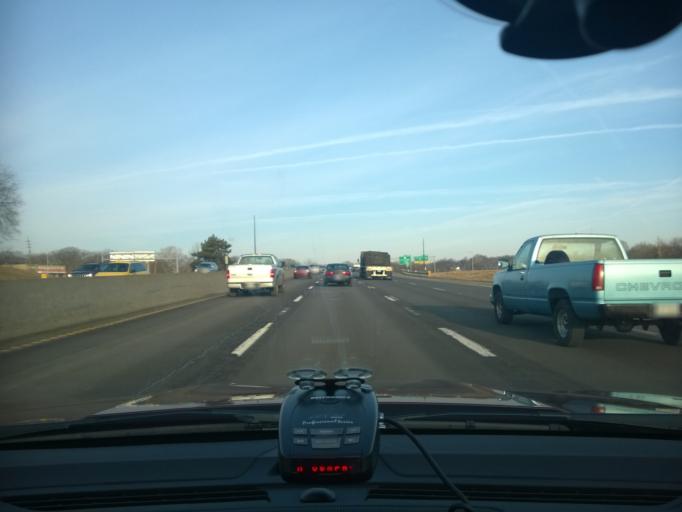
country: US
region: Missouri
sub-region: Saint Louis County
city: Pine Lawn
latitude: 38.7021
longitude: -90.2675
